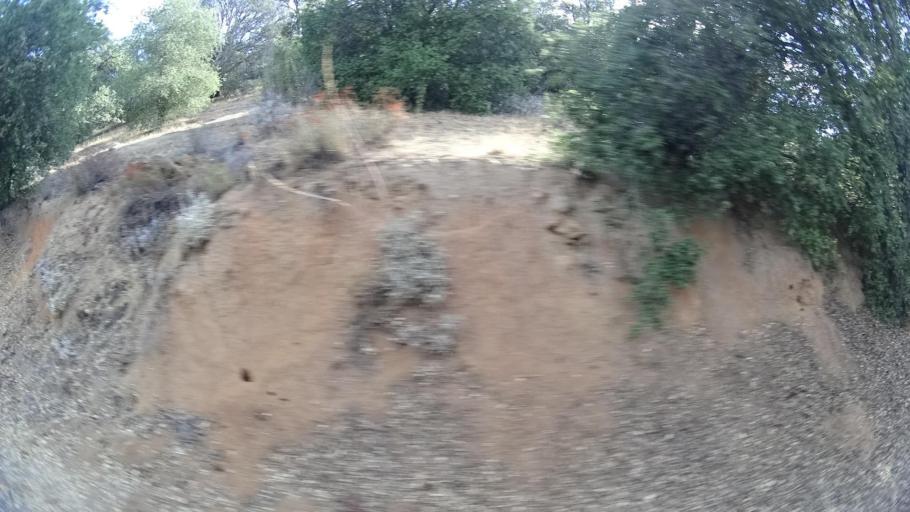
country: US
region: California
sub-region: San Diego County
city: Ramona
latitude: 33.1902
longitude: -116.7797
